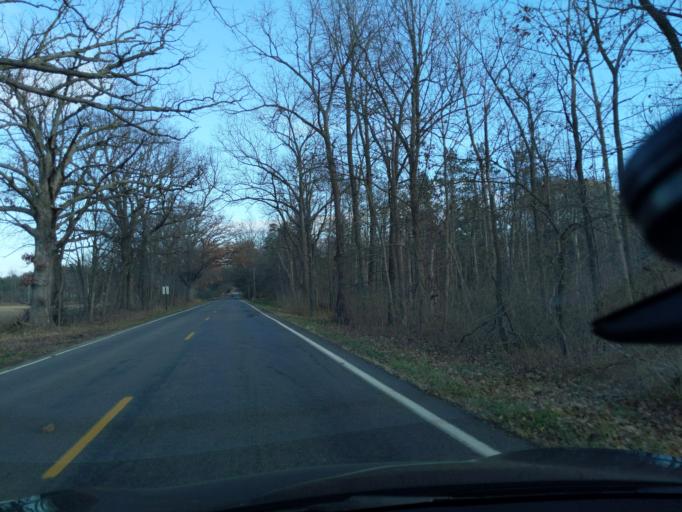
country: US
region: Michigan
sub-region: Ingham County
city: Haslett
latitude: 42.7154
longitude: -84.3490
